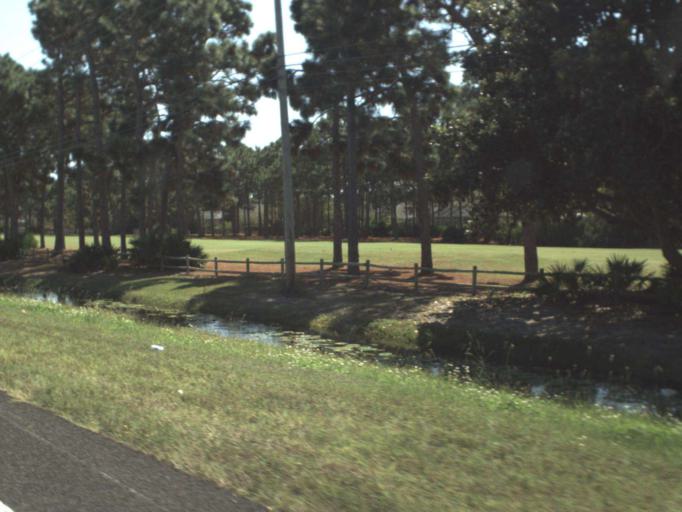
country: US
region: Florida
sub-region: Bay County
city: Panama City Beach
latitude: 30.1923
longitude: -85.7989
